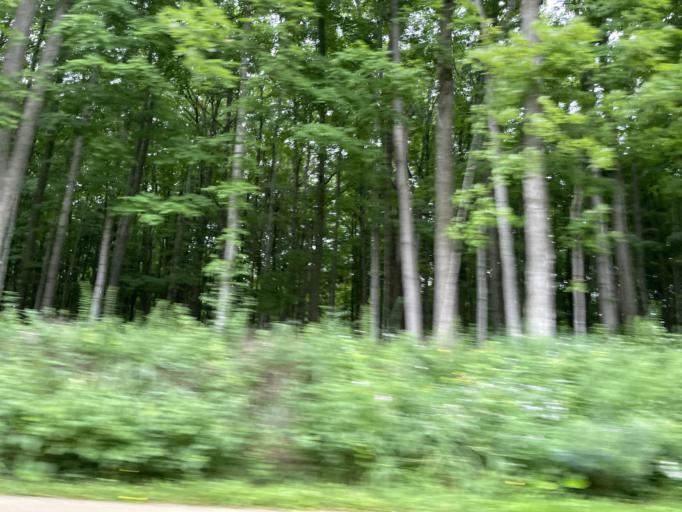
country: CA
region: Ontario
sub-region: Wellington County
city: Guelph
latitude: 43.5125
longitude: -80.2224
